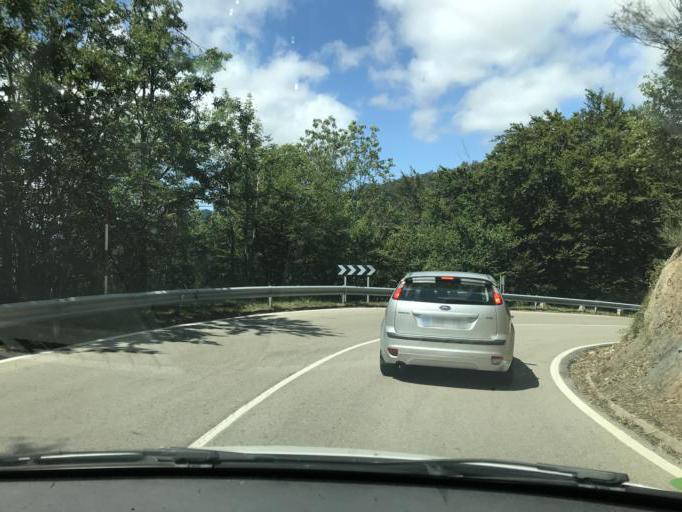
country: ES
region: Cantabria
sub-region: Provincia de Cantabria
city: Cabezon de Liebana
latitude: 43.0740
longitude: -4.4754
